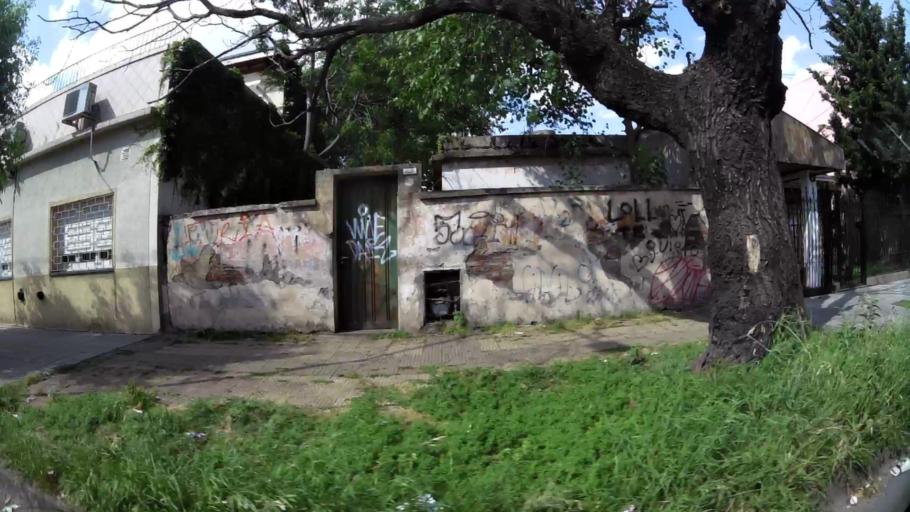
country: AR
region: Buenos Aires
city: San Justo
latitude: -34.6426
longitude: -58.5531
